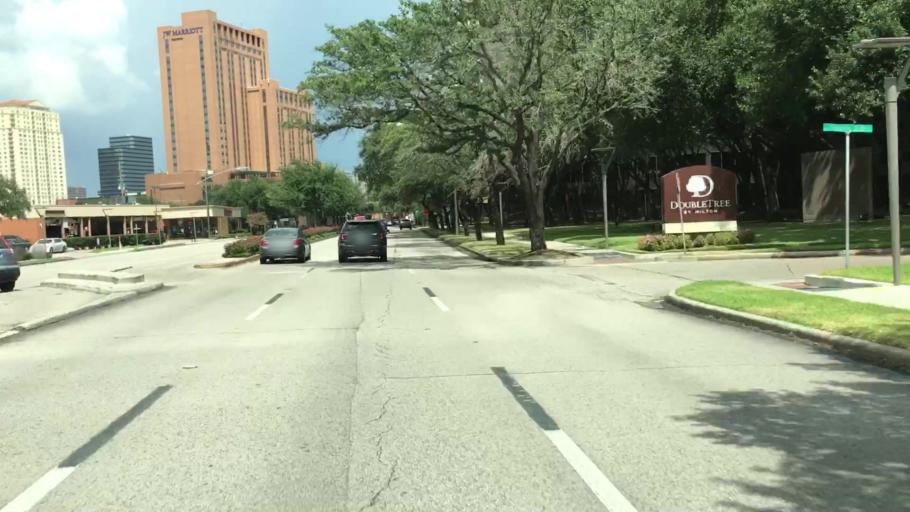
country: US
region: Texas
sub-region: Harris County
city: Bellaire
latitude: 29.7395
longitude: -95.4696
